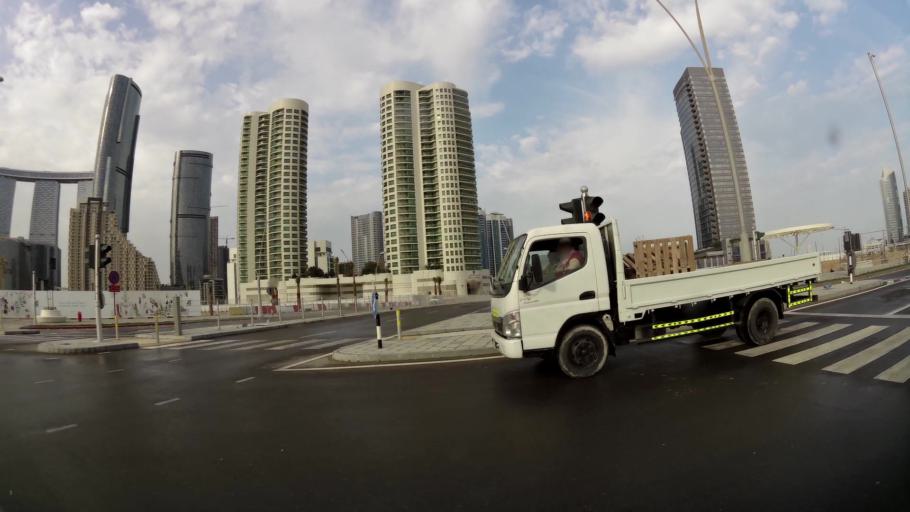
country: AE
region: Abu Dhabi
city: Abu Dhabi
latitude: 24.5004
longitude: 54.4130
